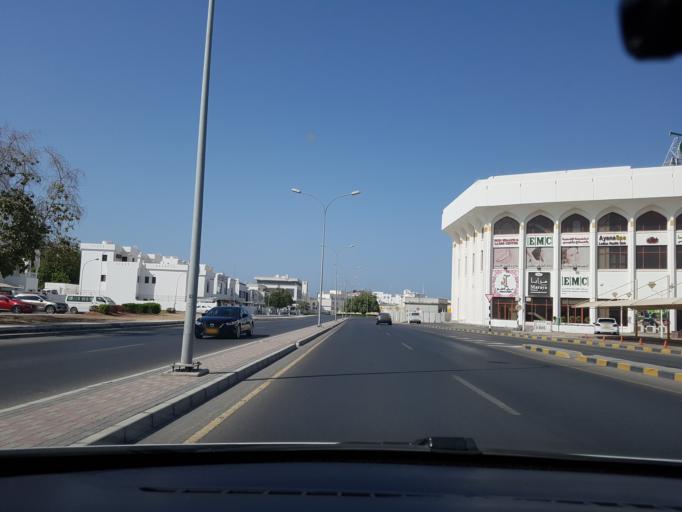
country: OM
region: Muhafazat Masqat
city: Bawshar
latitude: 23.6060
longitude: 58.4526
